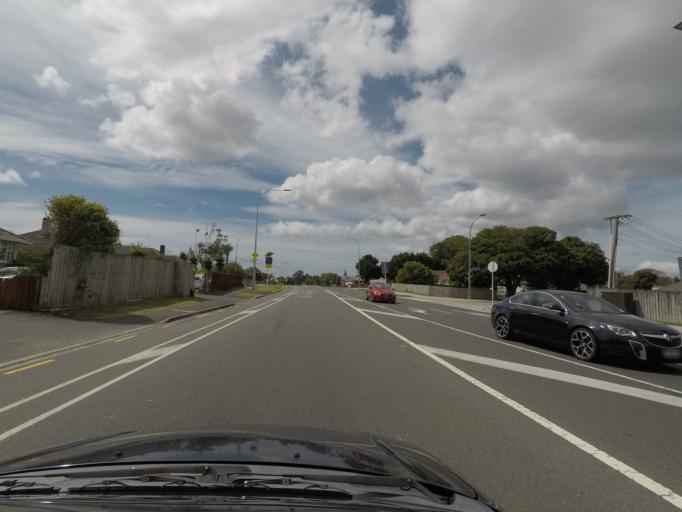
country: NZ
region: Auckland
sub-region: Auckland
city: Auckland
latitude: -36.9038
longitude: 174.7285
